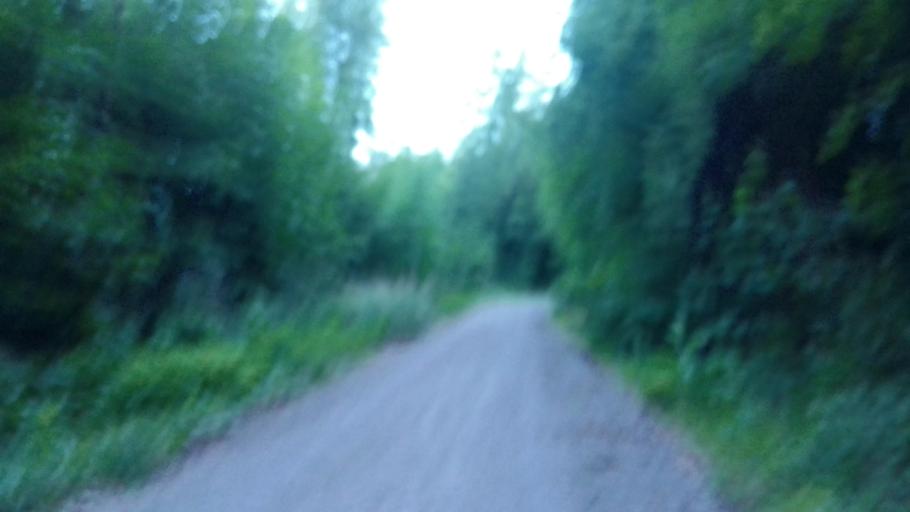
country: DE
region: Lower Saxony
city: Salzhemmendorf
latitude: 52.0273
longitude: 9.5851
